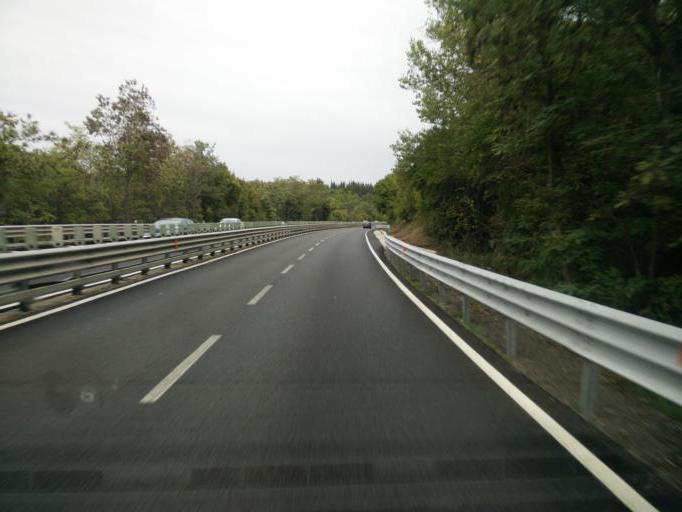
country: IT
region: Tuscany
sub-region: Province of Florence
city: Barberino Val d'Elsa
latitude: 43.5227
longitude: 11.1990
